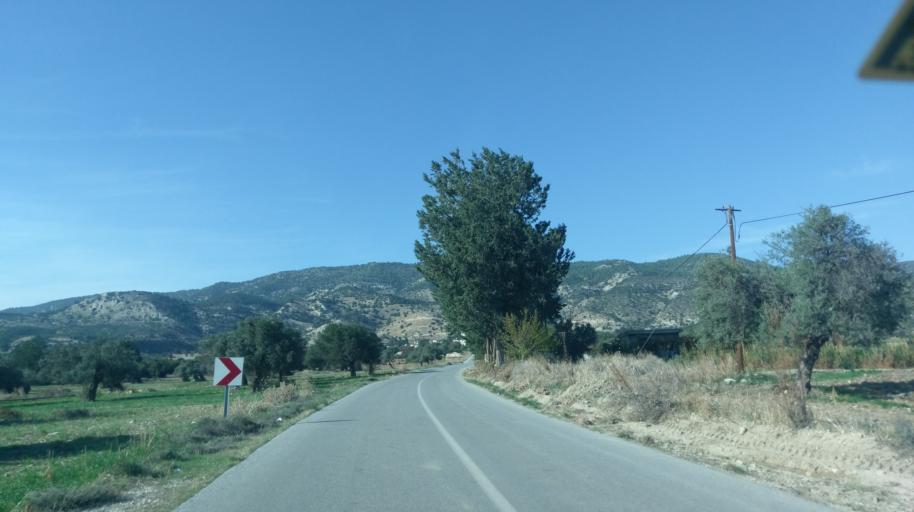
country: CY
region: Ammochostos
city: Trikomo
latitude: 35.3390
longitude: 33.8047
